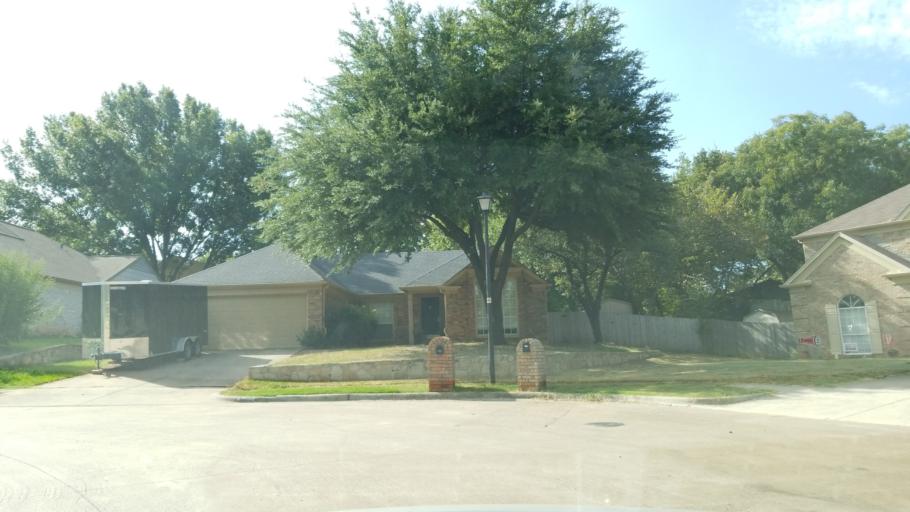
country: US
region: Texas
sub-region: Tarrant County
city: Grapevine
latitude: 32.8902
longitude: -97.0862
